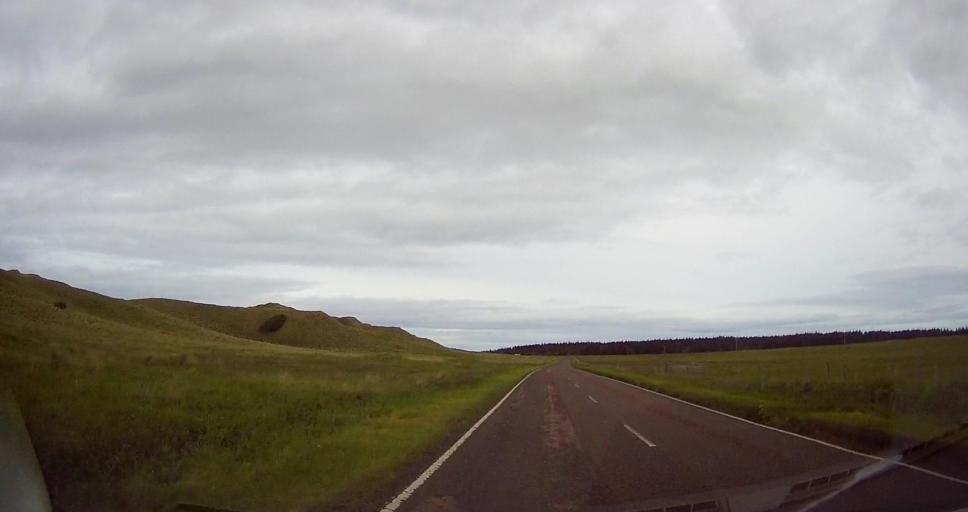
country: GB
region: Scotland
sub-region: Highland
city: Thurso
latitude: 58.6035
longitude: -3.3478
